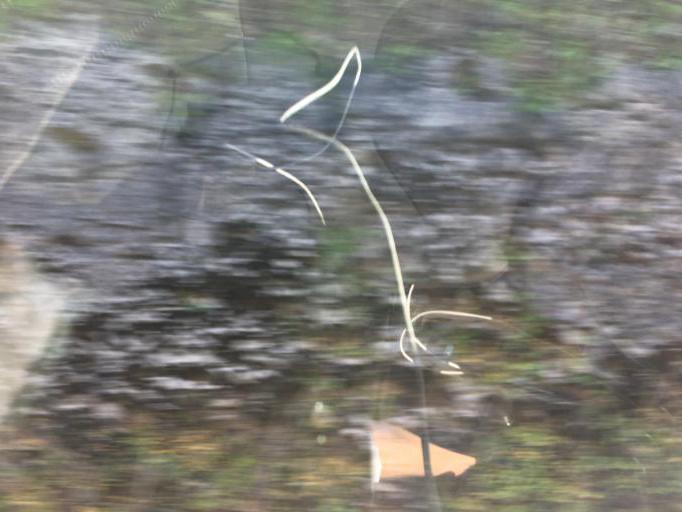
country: PT
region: Lisbon
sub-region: Sintra
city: Sintra
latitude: 38.8093
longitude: -9.3765
